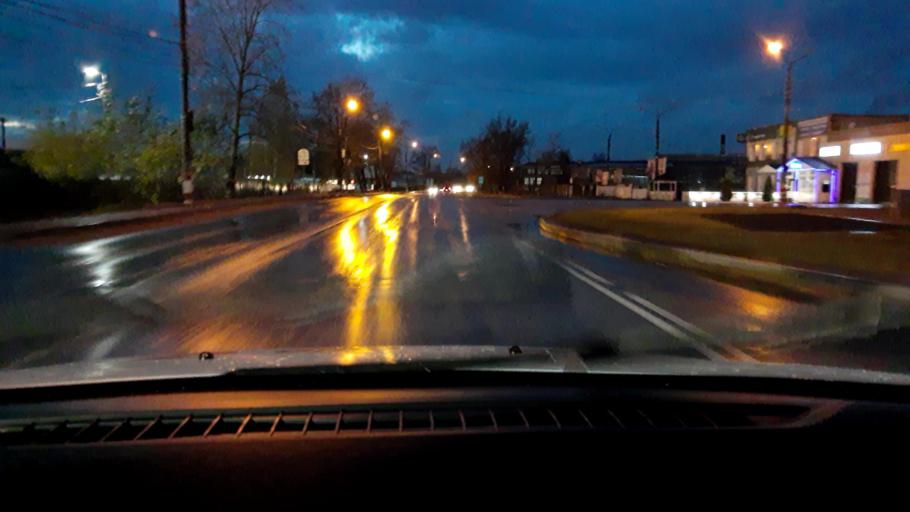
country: RU
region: Nizjnij Novgorod
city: Bor
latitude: 56.3465
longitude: 44.0846
